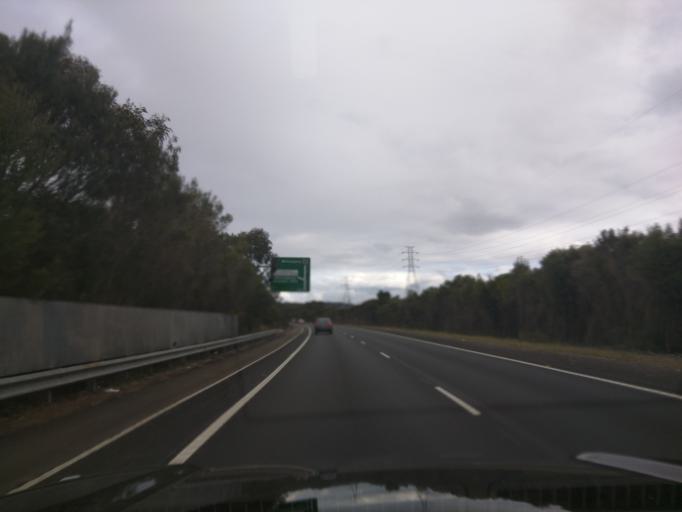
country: AU
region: New South Wales
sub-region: Wollongong
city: Helensburgh
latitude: -34.1890
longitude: 150.9680
